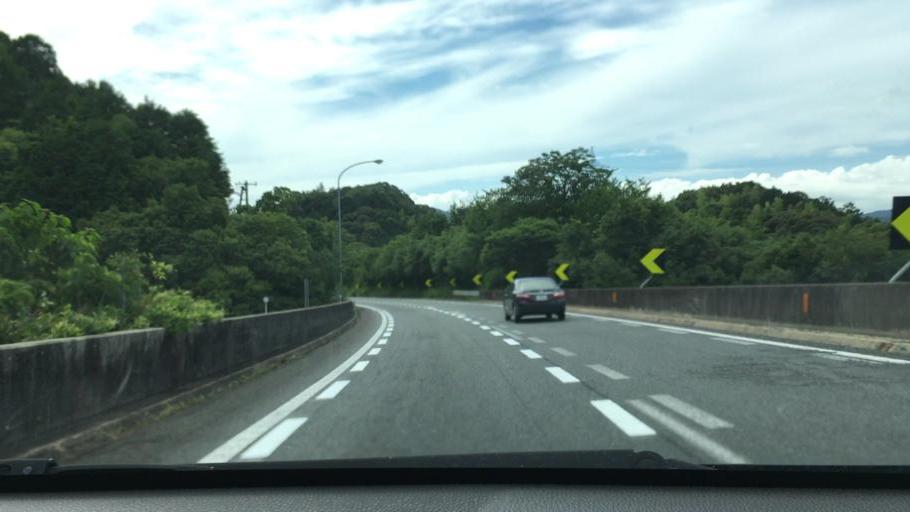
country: JP
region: Yamaguchi
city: Yamaguchi-shi
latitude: 34.1319
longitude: 131.4513
